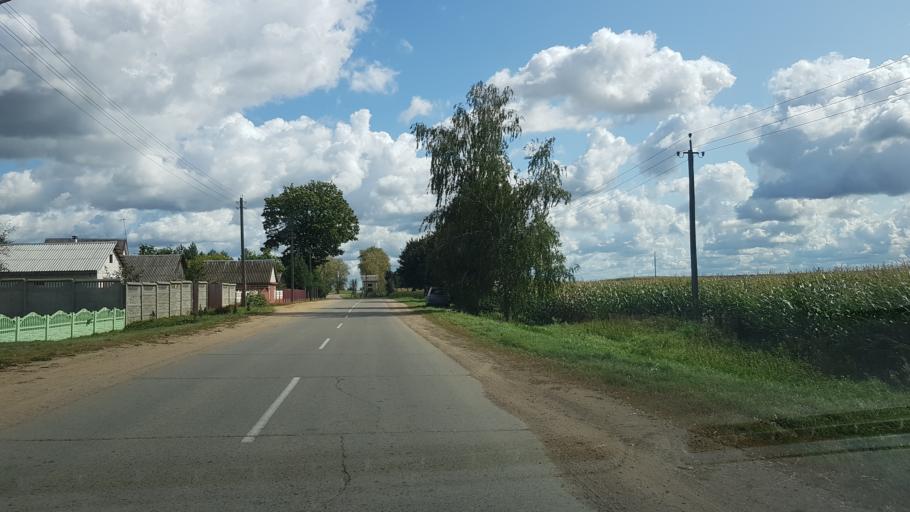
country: BY
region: Minsk
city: Dzyarzhynsk
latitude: 53.7367
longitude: 27.2086
